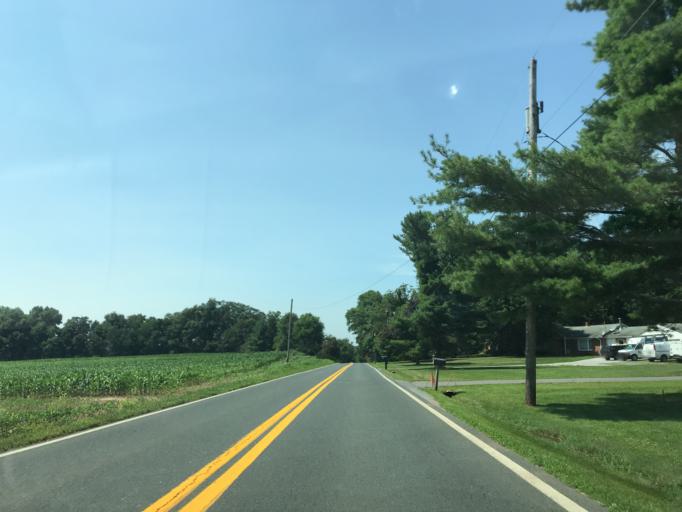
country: US
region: Maryland
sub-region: Carroll County
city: Taneytown
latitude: 39.6154
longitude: -77.1356
